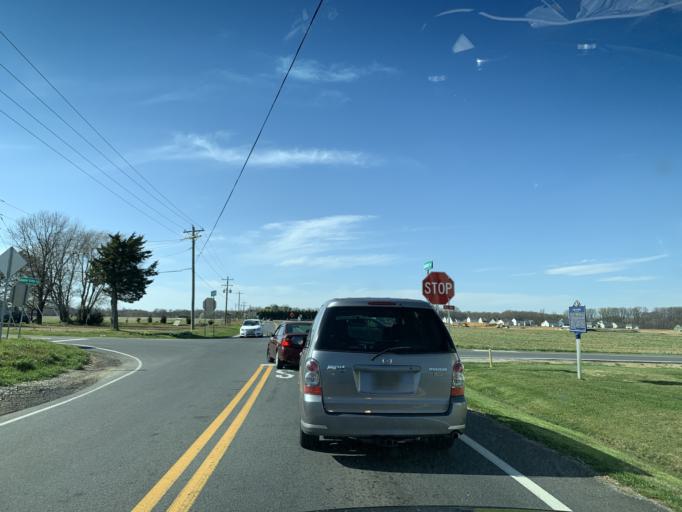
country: US
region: Delaware
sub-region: Kent County
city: Riverview
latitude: 38.9782
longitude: -75.5002
